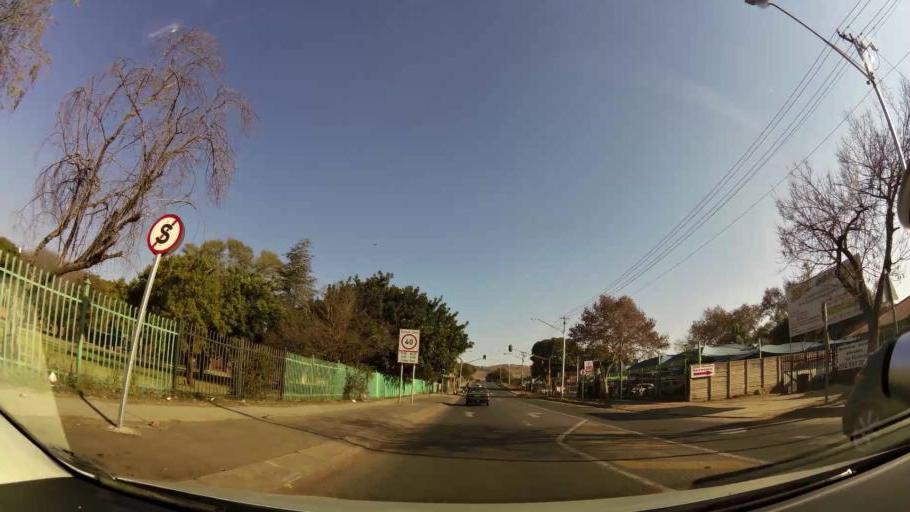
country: ZA
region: Gauteng
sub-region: City of Tshwane Metropolitan Municipality
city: Pretoria
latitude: -25.7156
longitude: 28.1554
